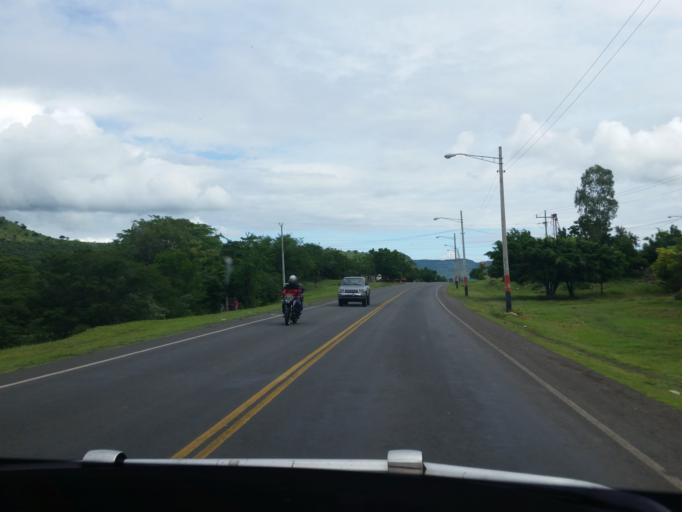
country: NI
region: Boaco
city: Teustepe
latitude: 12.4401
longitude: -86.0423
